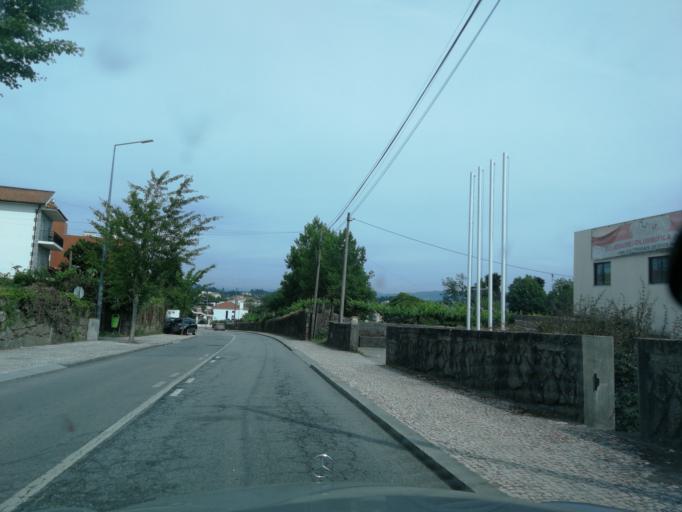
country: PT
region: Braga
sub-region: Vila Nova de Famalicao
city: Calendario
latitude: 41.4139
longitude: -8.5285
